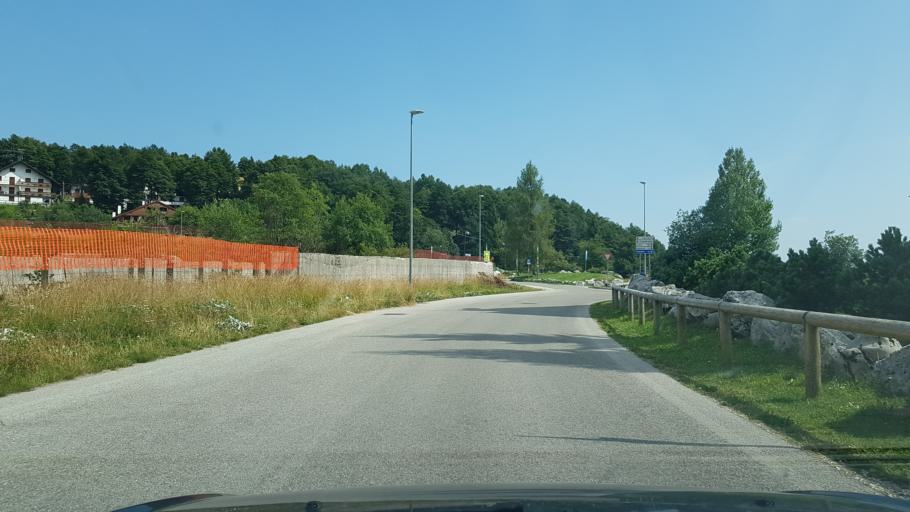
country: IT
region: Friuli Venezia Giulia
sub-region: Provincia di Pordenone
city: Budoia
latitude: 46.1085
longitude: 12.5197
